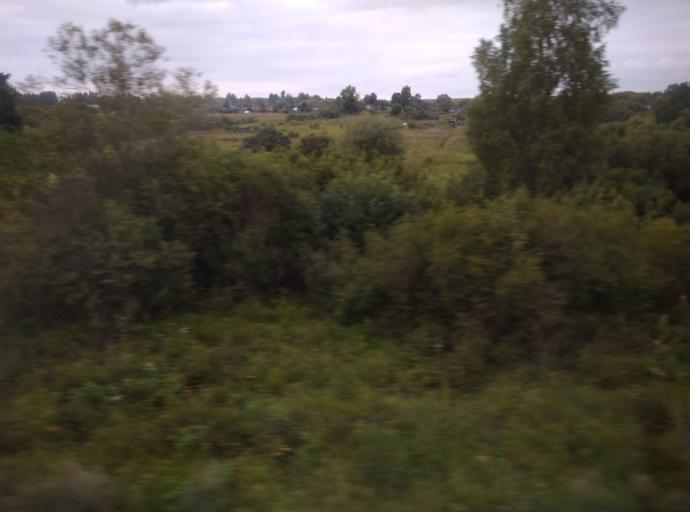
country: RU
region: Kostroma
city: Nerekhta
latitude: 57.4724
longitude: 40.5740
